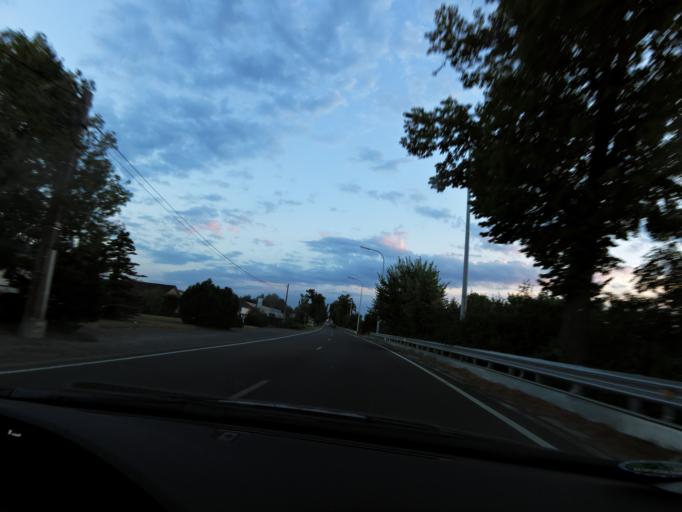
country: BE
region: Wallonia
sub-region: Province de Liege
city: Welkenraedt
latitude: 50.6923
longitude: 5.9631
